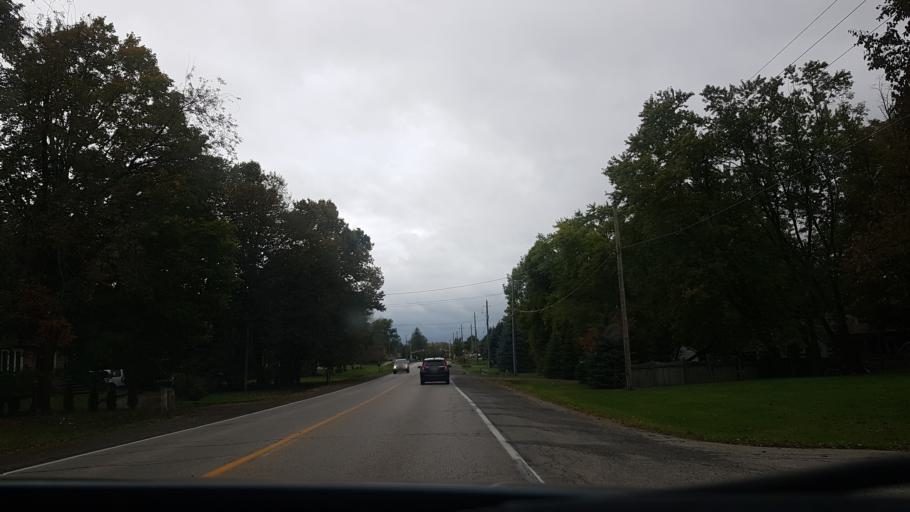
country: CA
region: Ontario
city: Uxbridge
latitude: 44.1041
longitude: -79.1045
